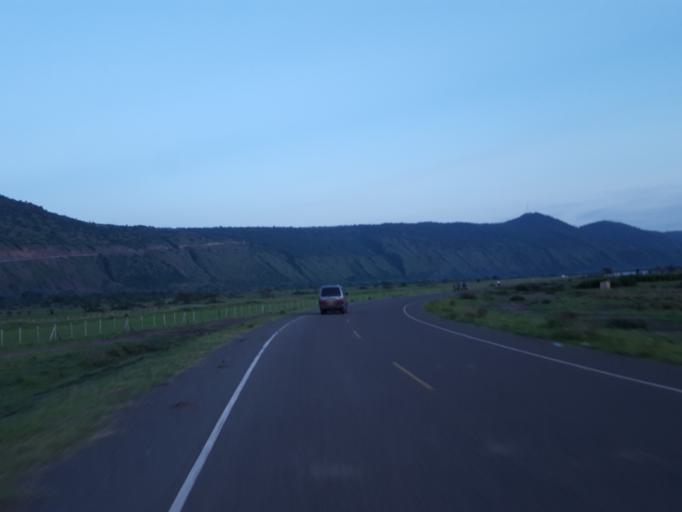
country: UG
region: Western Region
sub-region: Kibale District
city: Kagadi
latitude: 1.2513
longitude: 30.7484
